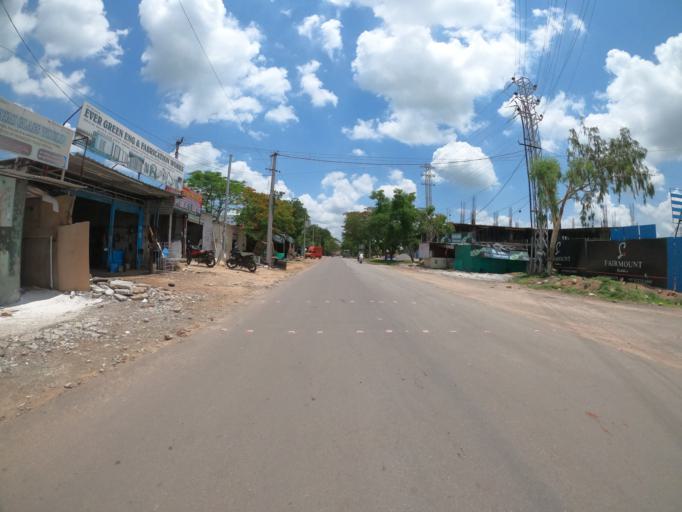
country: IN
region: Telangana
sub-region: Medak
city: Serilingampalle
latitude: 17.3852
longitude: 78.3308
